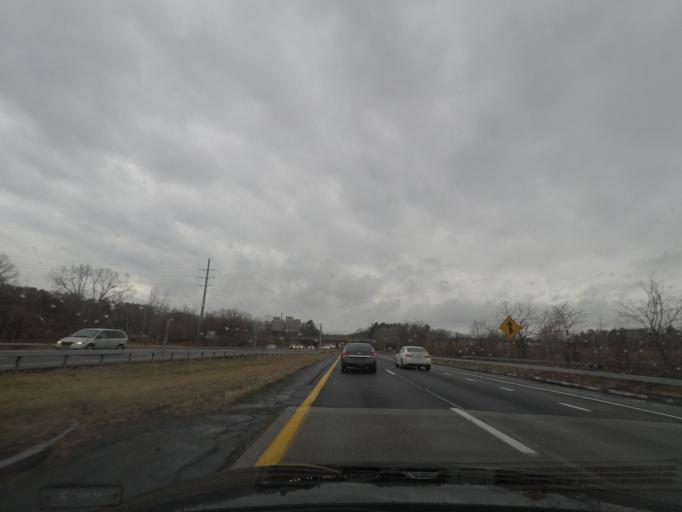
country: US
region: New York
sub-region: Albany County
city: McKownville
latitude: 42.6929
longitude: -73.8402
